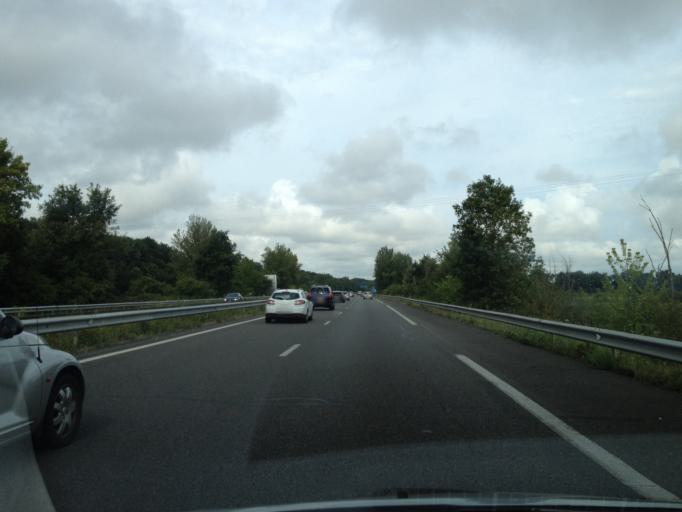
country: FR
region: Aquitaine
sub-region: Departement du Lot-et-Garonne
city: Layrac
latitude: 44.1231
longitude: 0.7091
